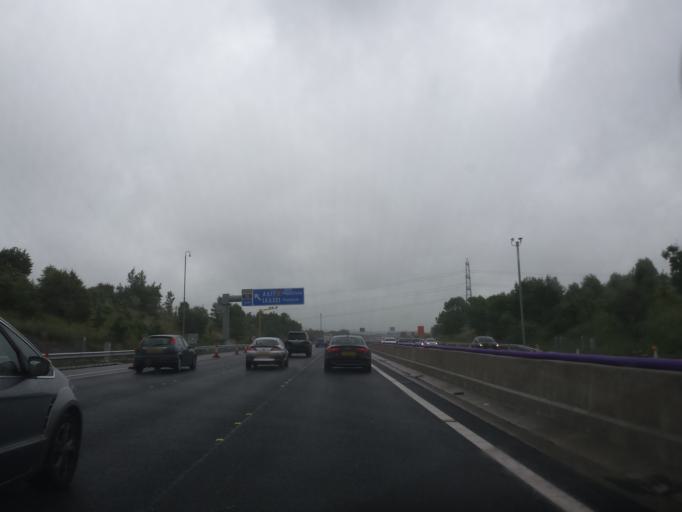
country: GB
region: England
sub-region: Derbyshire
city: Bolsover
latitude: 53.2129
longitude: -1.3236
